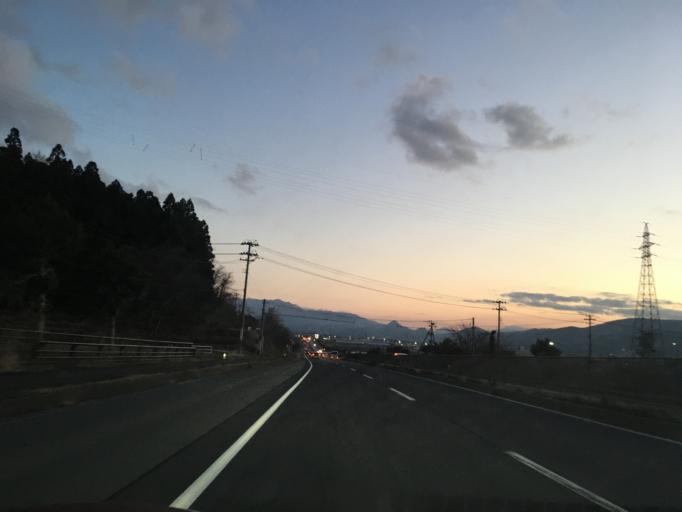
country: JP
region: Yamagata
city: Kaminoyama
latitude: 38.1615
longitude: 140.3019
